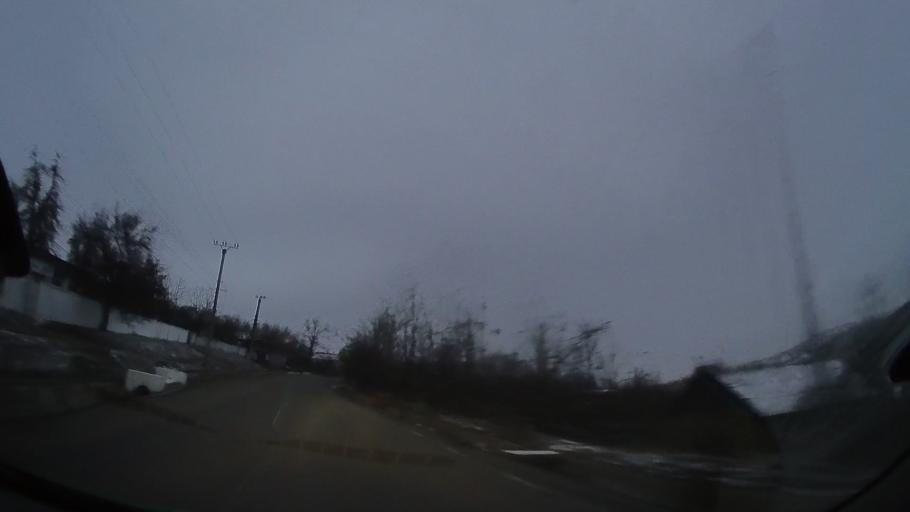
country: RO
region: Vaslui
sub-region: Comuna Vutcani
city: Vutcani
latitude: 46.4103
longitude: 27.9947
